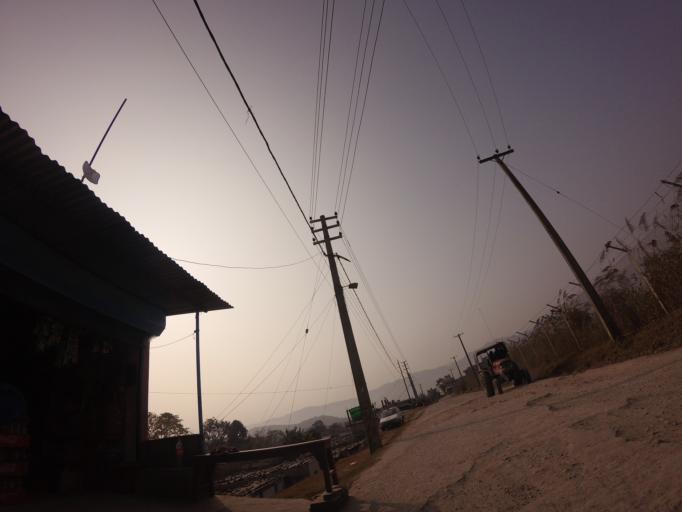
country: NP
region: Western Region
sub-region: Gandaki Zone
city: Pokhara
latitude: 28.2016
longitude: 83.9854
